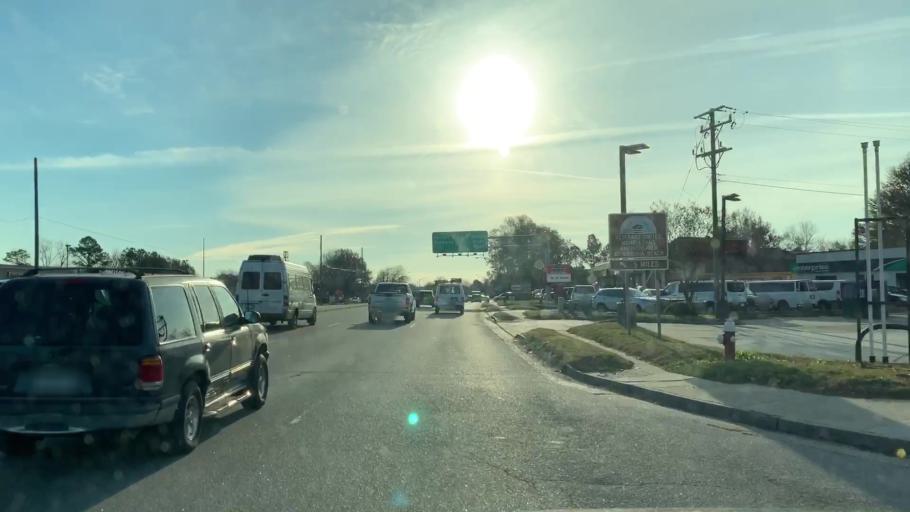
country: US
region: Virginia
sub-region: City of Chesapeake
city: Chesapeake
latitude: 36.7971
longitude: -76.1747
